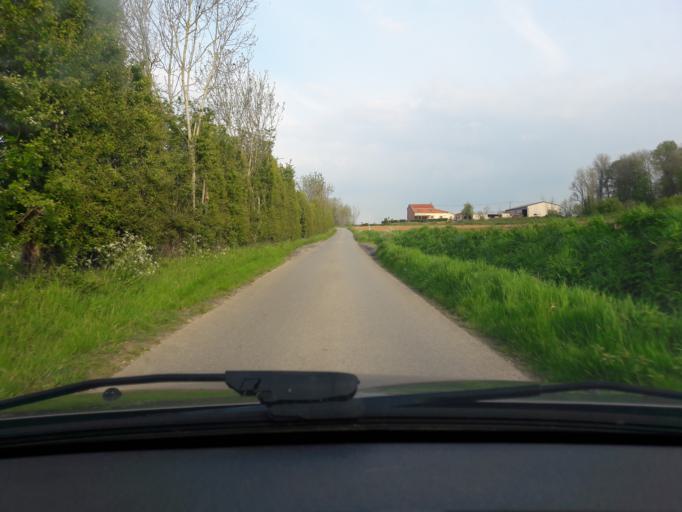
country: FR
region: Nord-Pas-de-Calais
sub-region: Departement du Nord
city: Marpent
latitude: 50.2478
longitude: 4.0769
